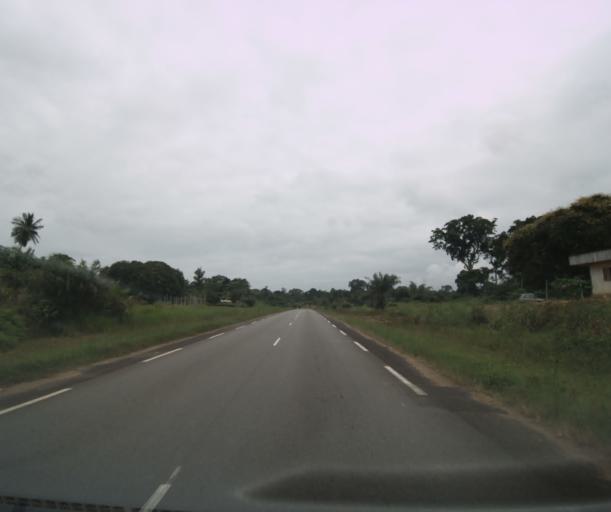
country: CM
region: South Province
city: Kribi
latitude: 3.1383
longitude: 10.0109
